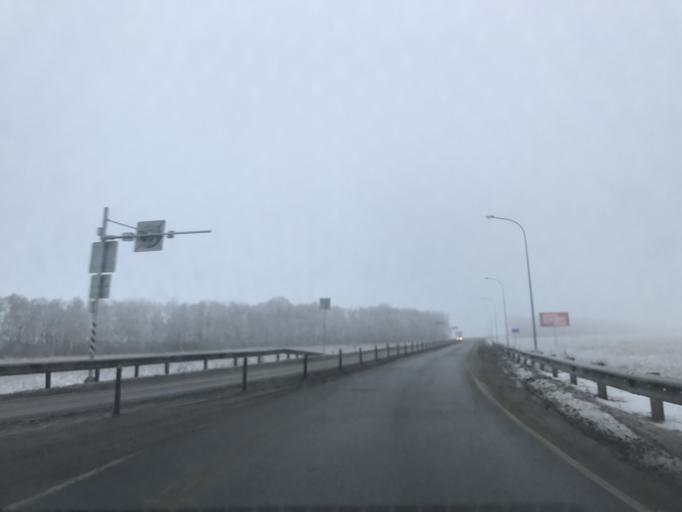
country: RU
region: Rostov
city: Temernik
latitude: 47.3670
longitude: 39.7240
